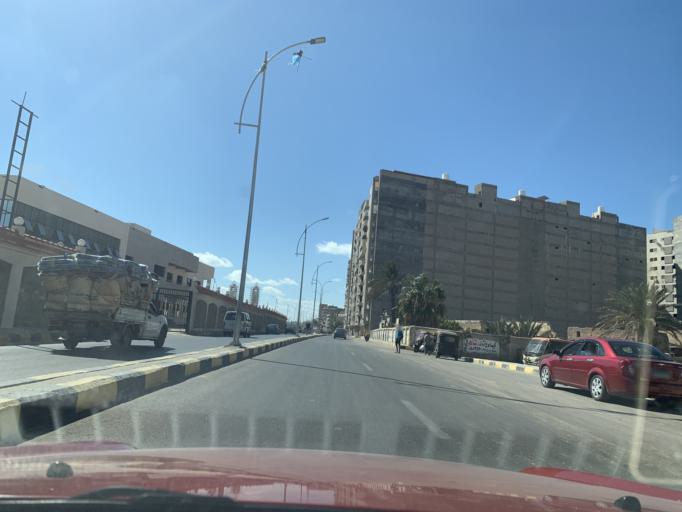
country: EG
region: Alexandria
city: Alexandria
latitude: 31.2236
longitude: 29.9746
